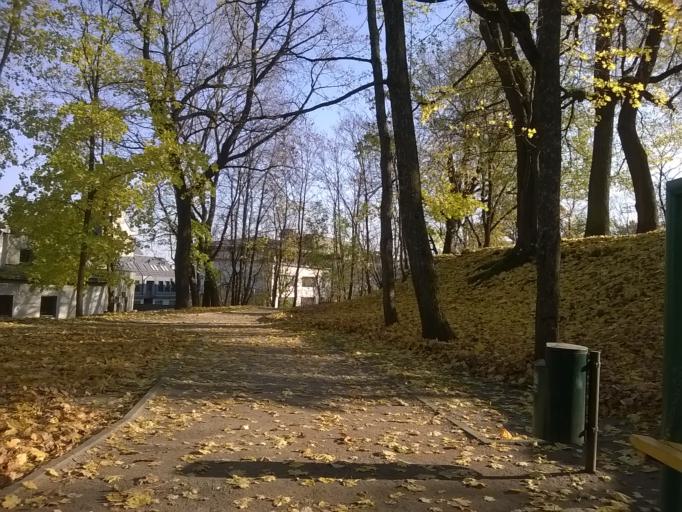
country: EE
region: Tartu
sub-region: Tartu linn
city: Tartu
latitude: 58.3785
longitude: 26.7218
